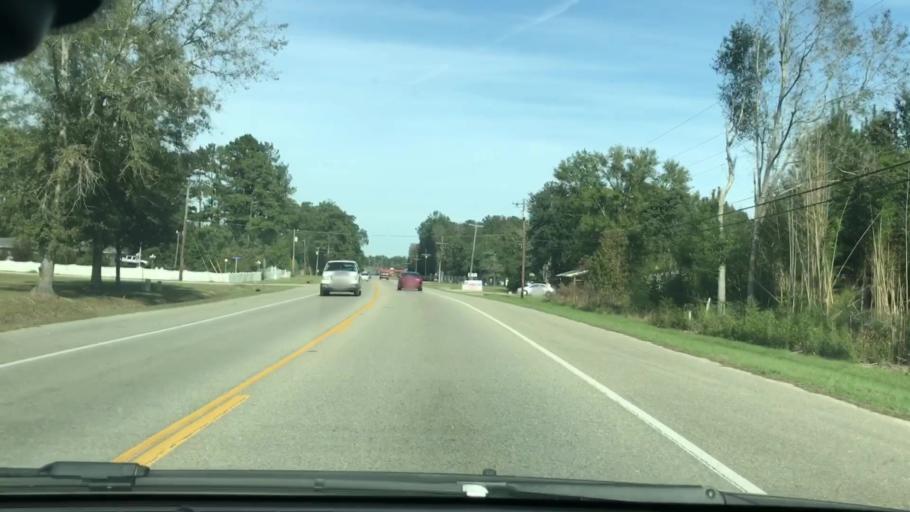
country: US
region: Louisiana
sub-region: Saint Tammany Parish
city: Pearl River
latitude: 30.3850
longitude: -89.7648
